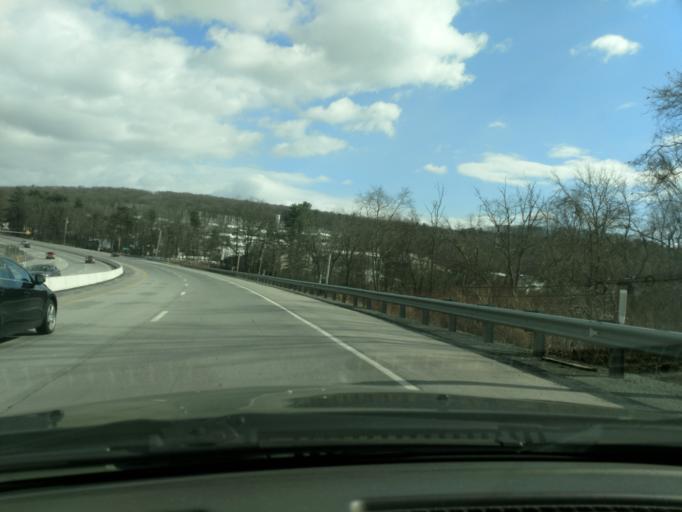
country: US
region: Pennsylvania
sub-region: Schuylkill County
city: Orwigsburg
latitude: 40.6192
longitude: -76.0578
